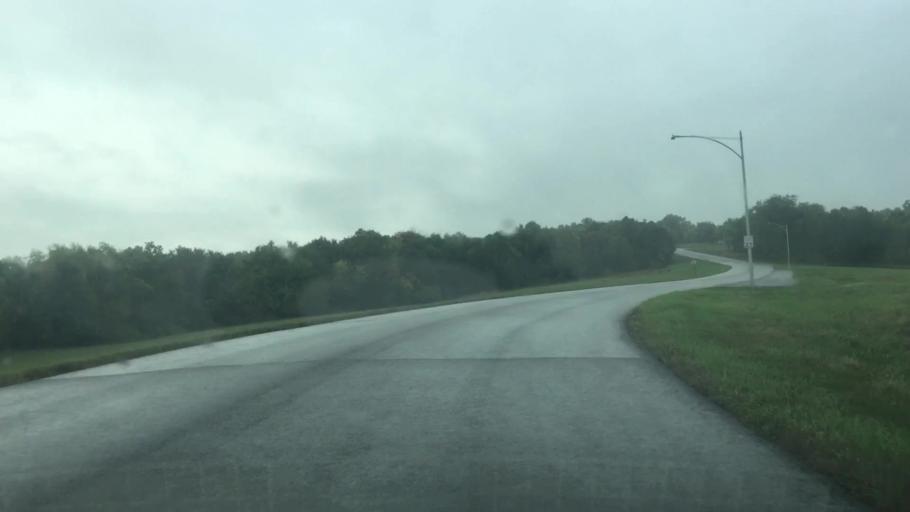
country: US
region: Kansas
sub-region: Johnson County
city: Lenexa
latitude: 38.9802
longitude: -94.8094
